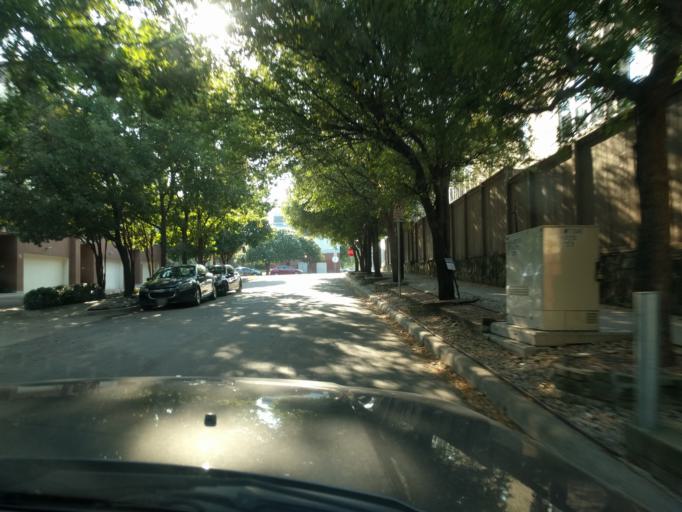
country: US
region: Texas
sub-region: Dallas County
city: Highland Park
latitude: 32.8126
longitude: -96.7953
